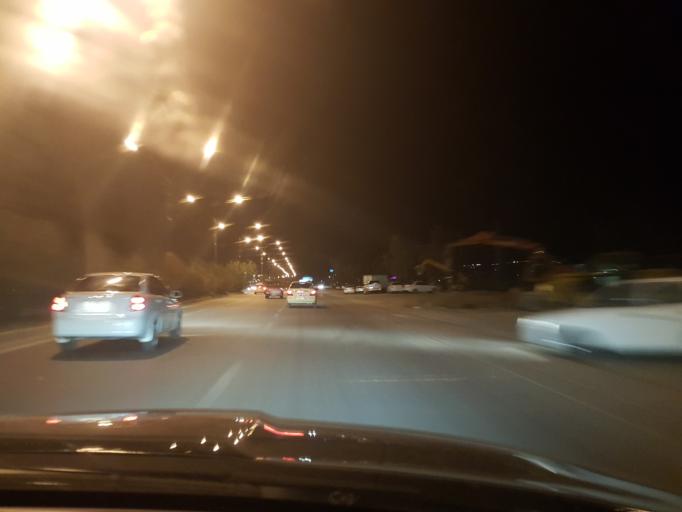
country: IQ
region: Arbil
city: Erbil
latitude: 36.2600
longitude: 44.0868
